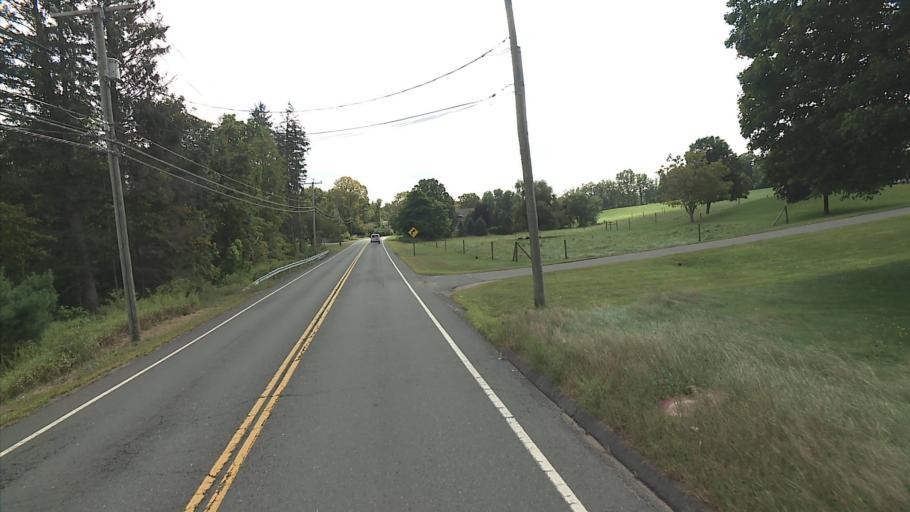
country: US
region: Connecticut
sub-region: Hartford County
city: North Granby
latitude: 41.9930
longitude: -72.8277
